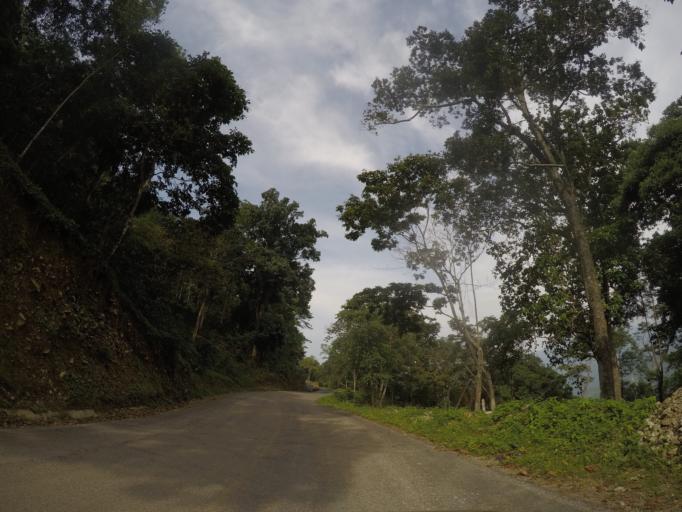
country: MX
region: Oaxaca
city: Pluma Hidalgo
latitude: 15.9446
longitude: -96.4415
